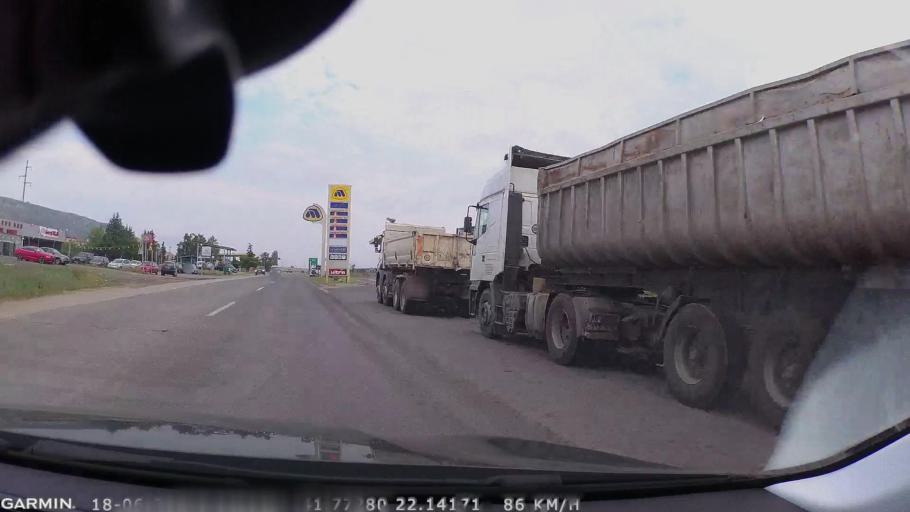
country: MK
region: Stip
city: Shtip
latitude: 41.7733
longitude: 22.1406
